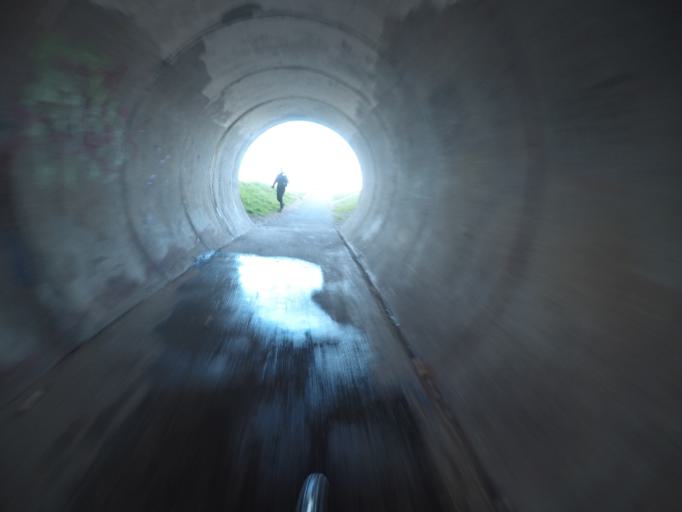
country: GB
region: Scotland
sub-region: North Ayrshire
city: Kilwinning
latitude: 55.6503
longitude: -4.7068
